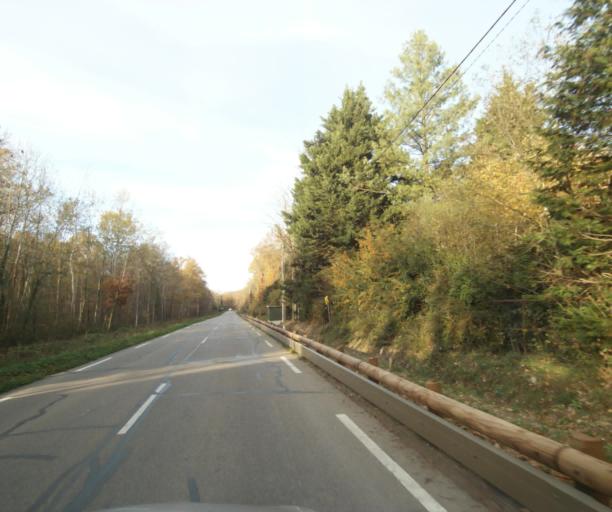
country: FR
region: Ile-de-France
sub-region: Departement des Yvelines
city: Chanteloup-les-Vignes
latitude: 48.9870
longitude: 2.0254
